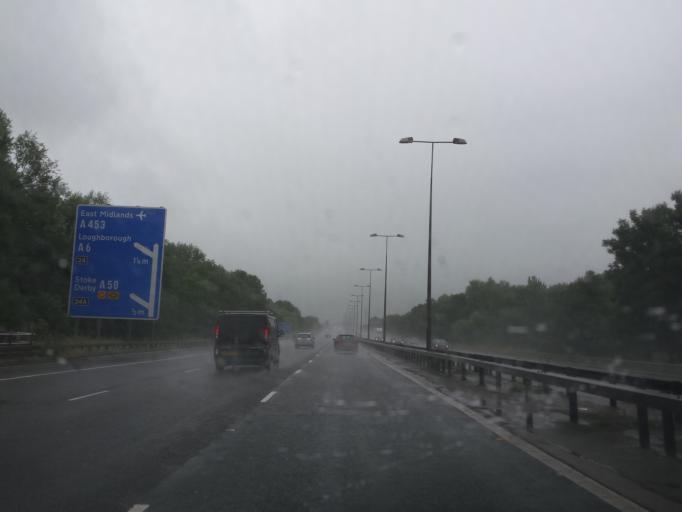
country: GB
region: England
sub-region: Leicestershire
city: Kegworth
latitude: 52.8668
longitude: -1.3056
